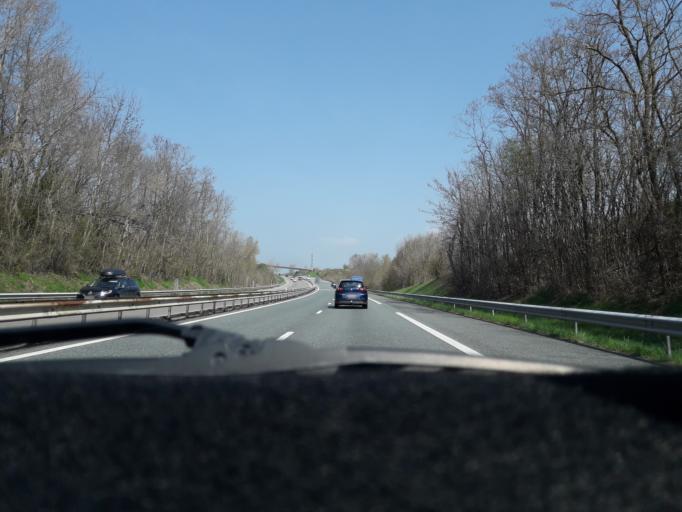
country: FR
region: Rhone-Alpes
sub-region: Departement de l'Isere
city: Saint-Victor-de-Cessieu
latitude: 45.5211
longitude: 5.4102
